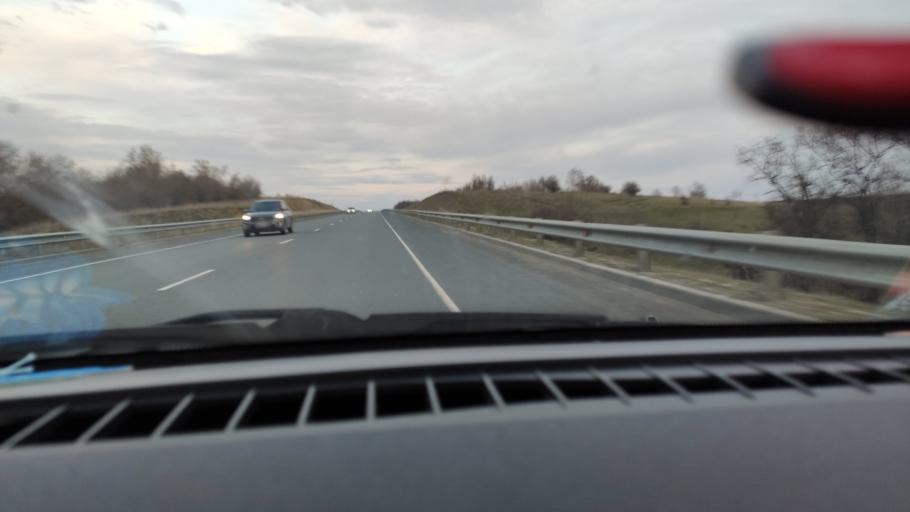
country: RU
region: Saratov
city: Yelshanka
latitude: 51.8214
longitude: 46.3372
